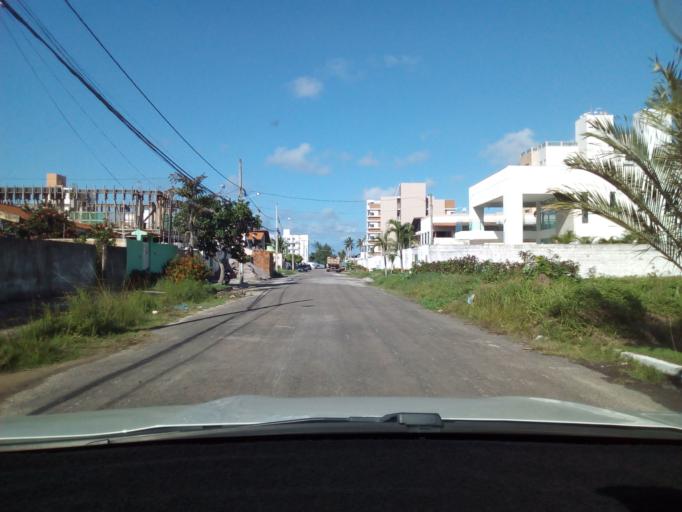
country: BR
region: Paraiba
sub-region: Joao Pessoa
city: Joao Pessoa
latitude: -7.0533
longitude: -34.8458
